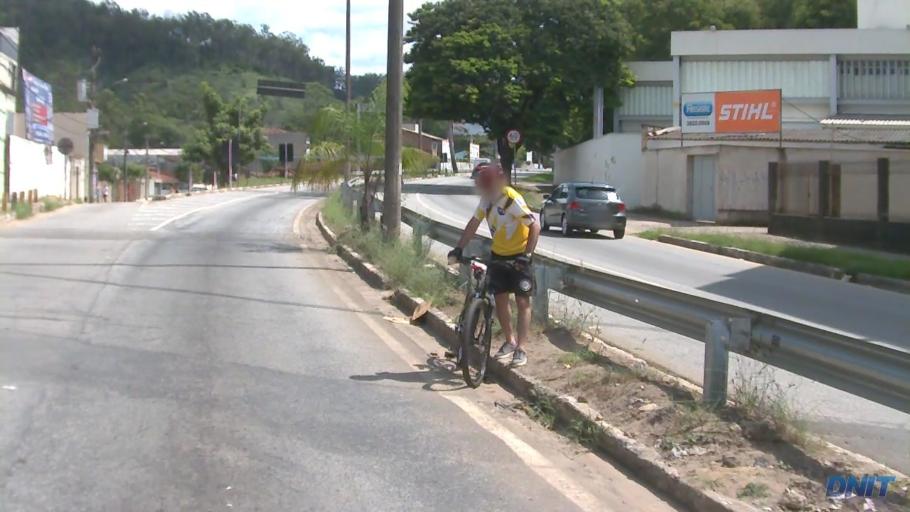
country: BR
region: Minas Gerais
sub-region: Coronel Fabriciano
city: Coronel Fabriciano
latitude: -19.5100
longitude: -42.5748
